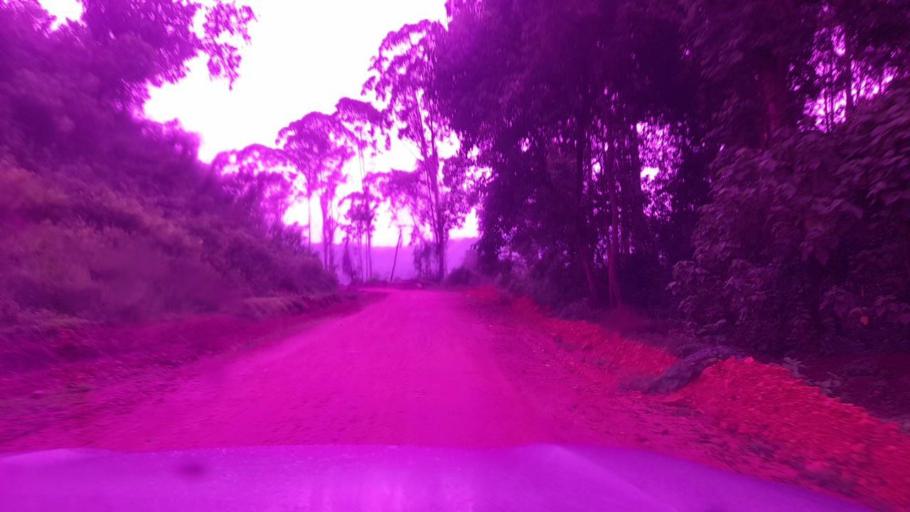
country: ET
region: Southern Nations, Nationalities, and People's Region
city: Bonga
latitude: 7.4492
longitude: 36.1461
